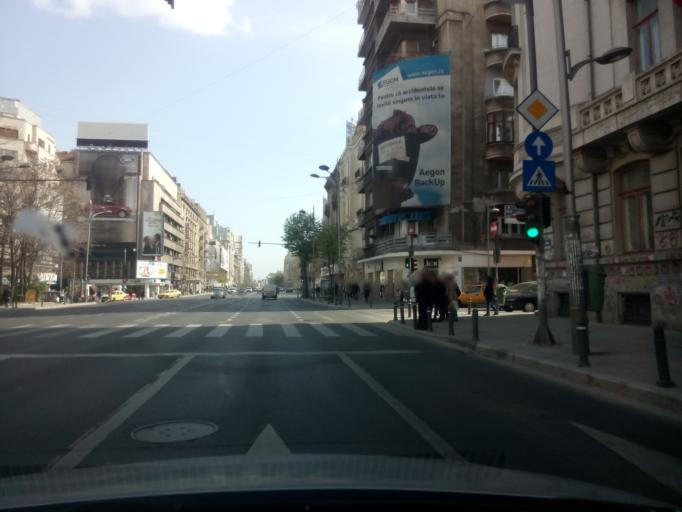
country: RO
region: Bucuresti
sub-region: Municipiul Bucuresti
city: Bucharest
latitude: 44.4448
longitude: 26.0977
